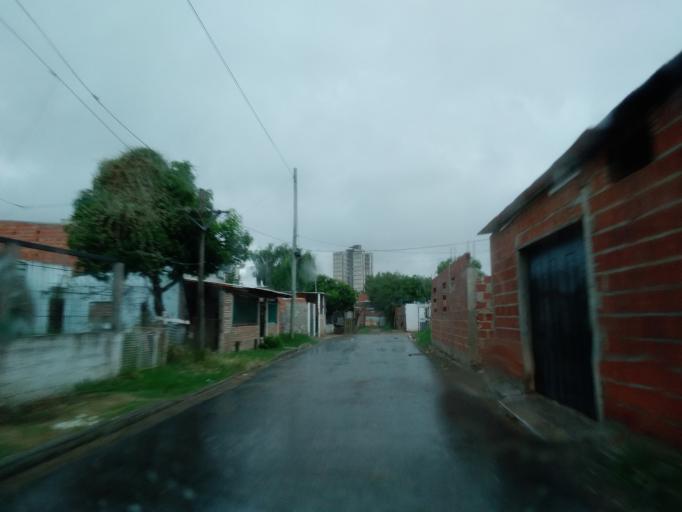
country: AR
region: Corrientes
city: Corrientes
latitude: -27.4894
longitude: -58.8227
